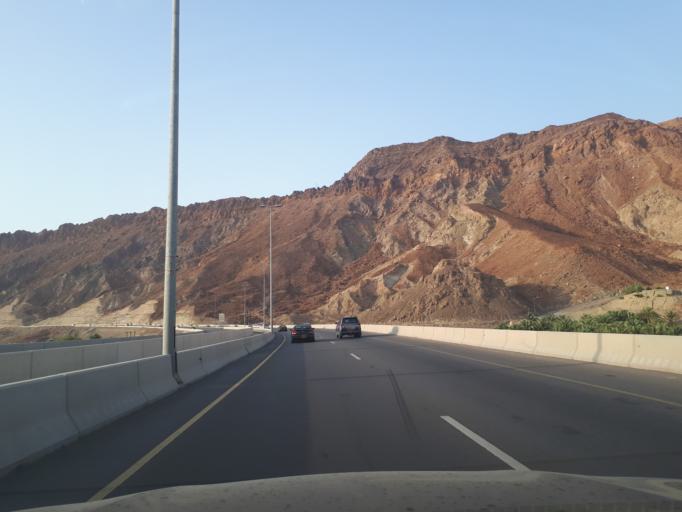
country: OM
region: Muhafazat ad Dakhiliyah
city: Bidbid
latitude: 23.4450
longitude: 58.1225
